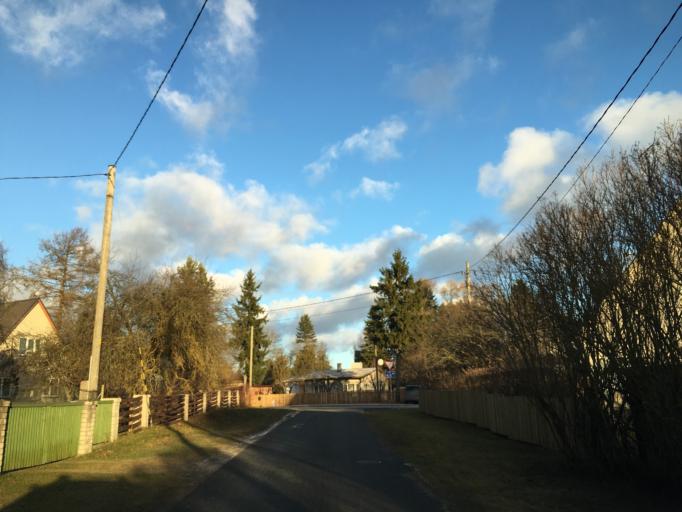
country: EE
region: Harju
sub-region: Saue linn
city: Saue
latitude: 59.3215
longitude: 24.5522
